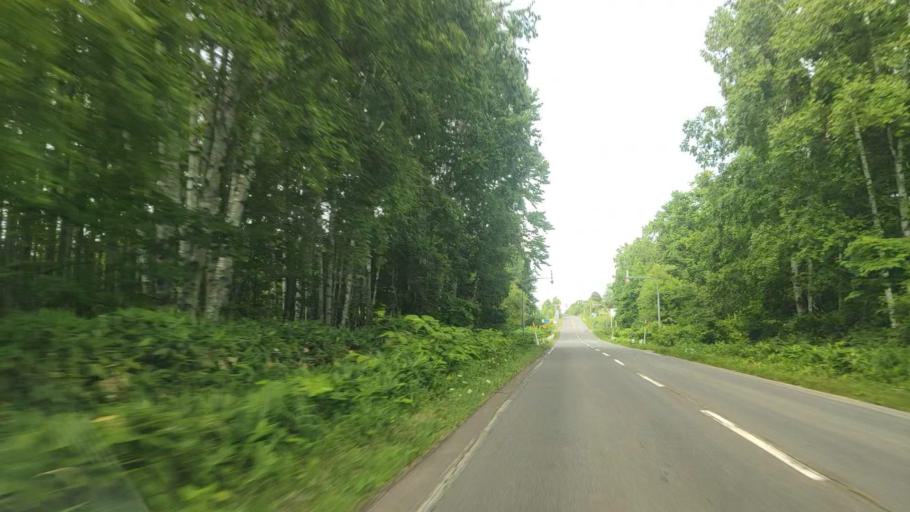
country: JP
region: Hokkaido
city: Nayoro
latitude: 44.2446
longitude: 142.4156
